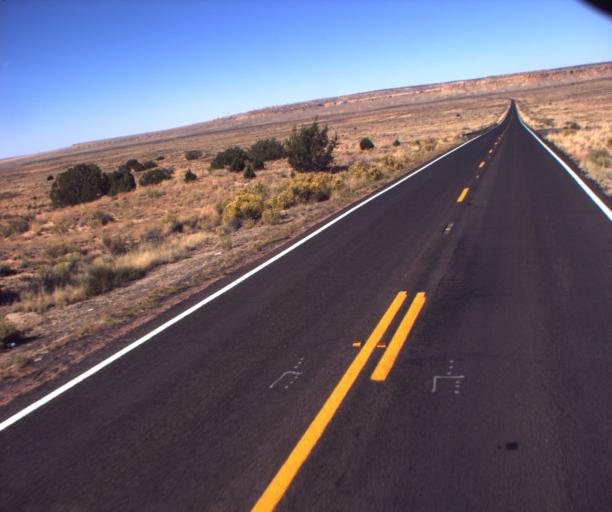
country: US
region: Arizona
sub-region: Navajo County
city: First Mesa
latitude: 35.9628
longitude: -110.6887
